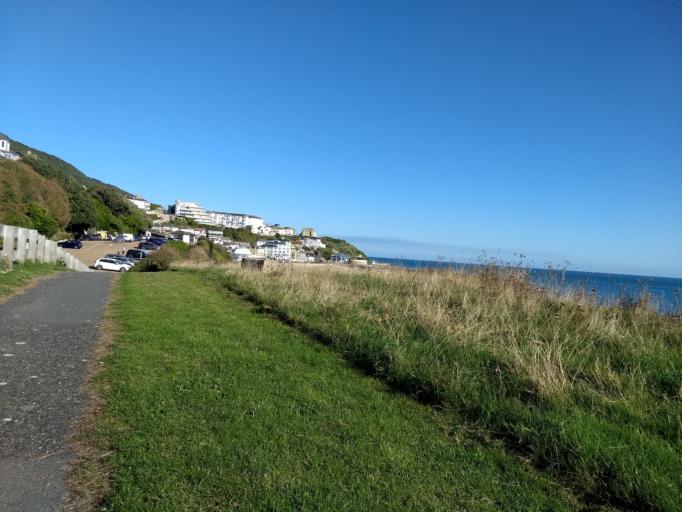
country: GB
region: England
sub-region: Isle of Wight
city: Ventnor
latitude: 50.5919
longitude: -1.2132
